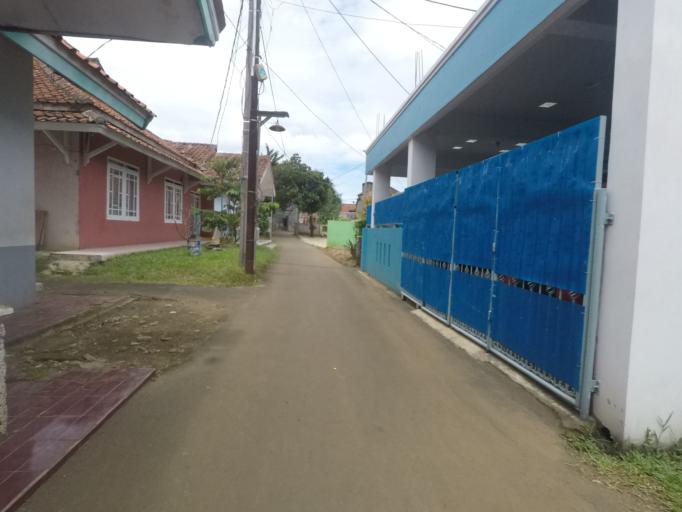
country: ID
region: West Java
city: Ciampea
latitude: -6.5492
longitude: 106.7473
